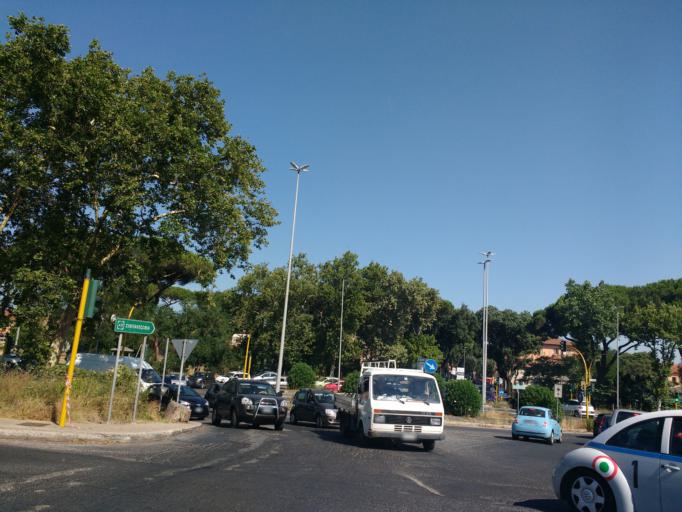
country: IT
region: Latium
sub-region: Citta metropolitana di Roma Capitale
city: Acilia-Castel Fusano-Ostia Antica
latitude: 41.7592
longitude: 12.3042
